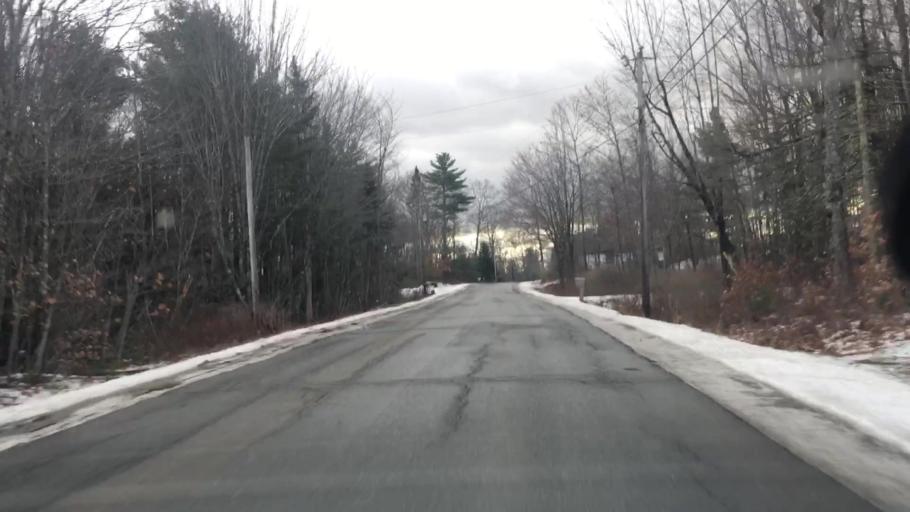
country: US
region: Maine
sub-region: Hancock County
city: Dedham
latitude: 44.6394
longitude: -68.7045
